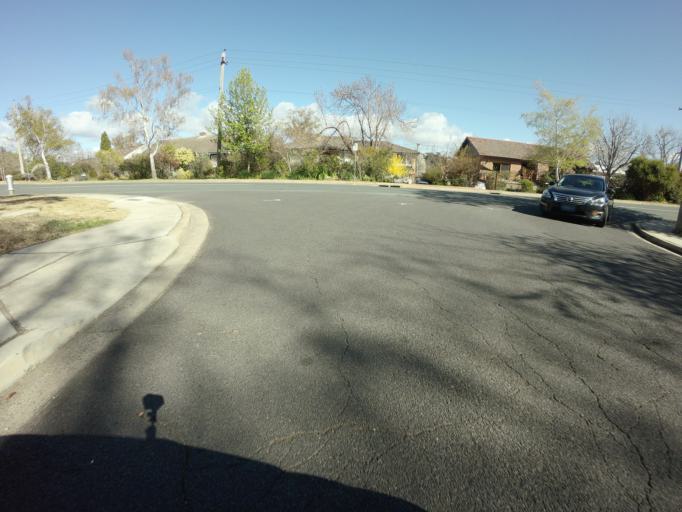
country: AU
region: Australian Capital Territory
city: Canberra
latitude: -35.2876
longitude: 149.1477
